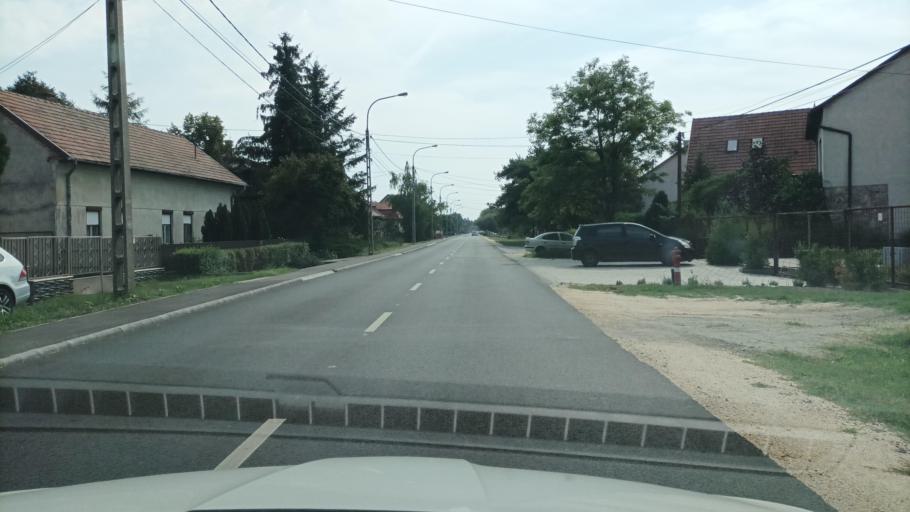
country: HU
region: Pest
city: Tura
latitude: 47.6214
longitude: 19.5973
